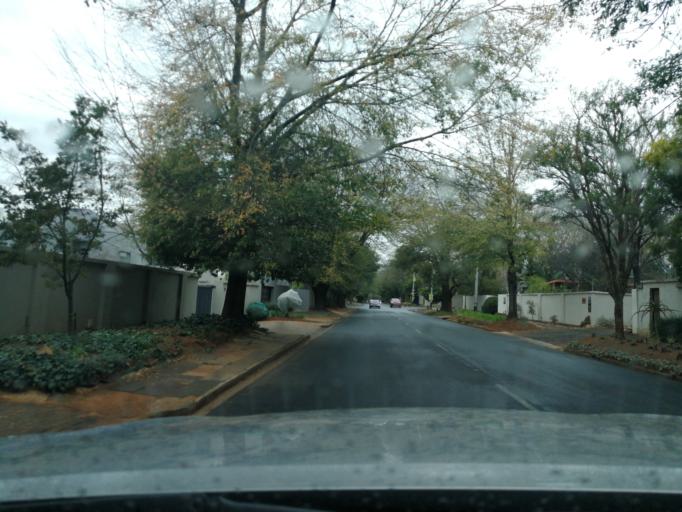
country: ZA
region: Gauteng
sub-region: City of Johannesburg Metropolitan Municipality
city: Johannesburg
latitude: -26.1560
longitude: 28.0169
